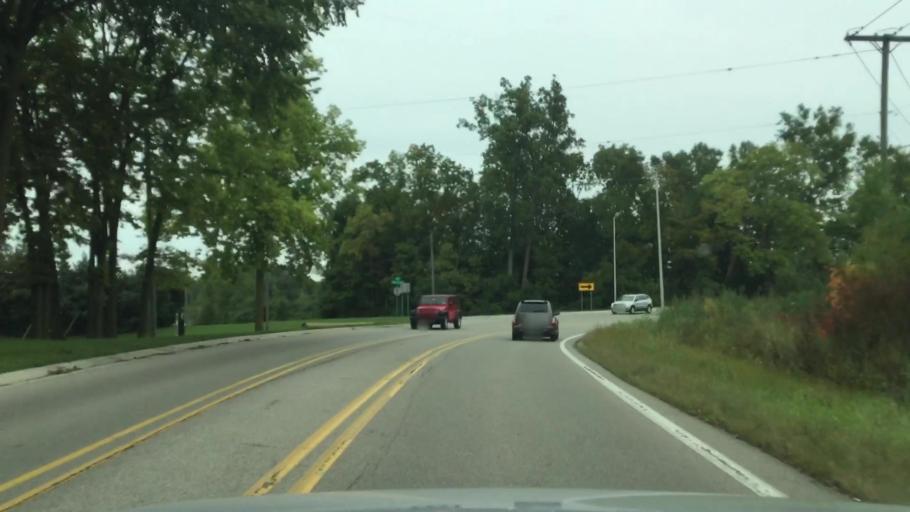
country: US
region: Michigan
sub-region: Washtenaw County
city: Ypsilanti
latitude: 42.2088
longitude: -83.6211
